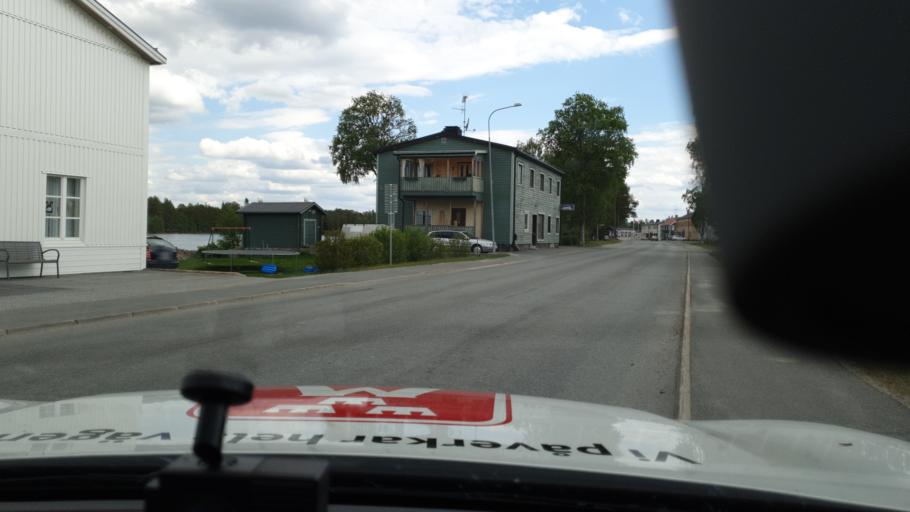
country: SE
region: Vaesterbotten
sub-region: Sorsele Kommun
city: Sorsele
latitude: 65.5392
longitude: 17.5225
